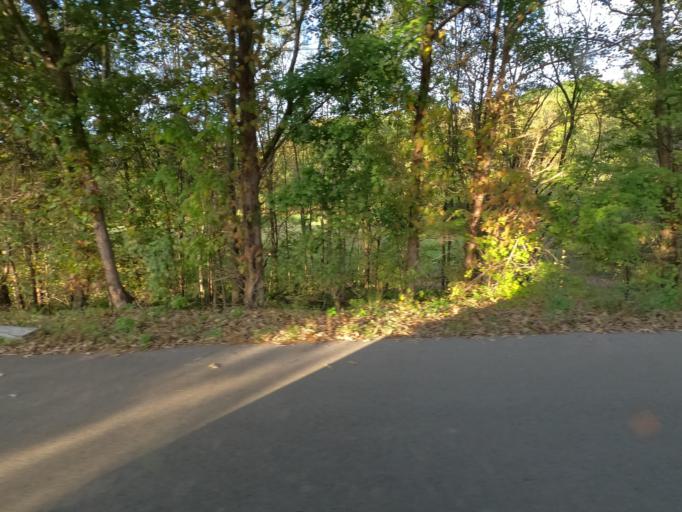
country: US
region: Tennessee
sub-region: Humphreys County
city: Waverly
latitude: 35.8819
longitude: -87.7967
